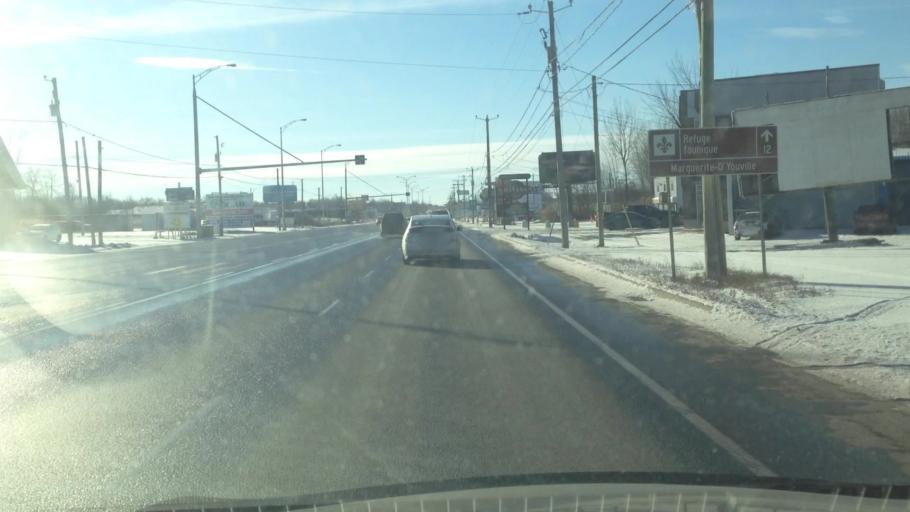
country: CA
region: Quebec
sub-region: Monteregie
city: Chateauguay
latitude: 45.3718
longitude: -73.7083
